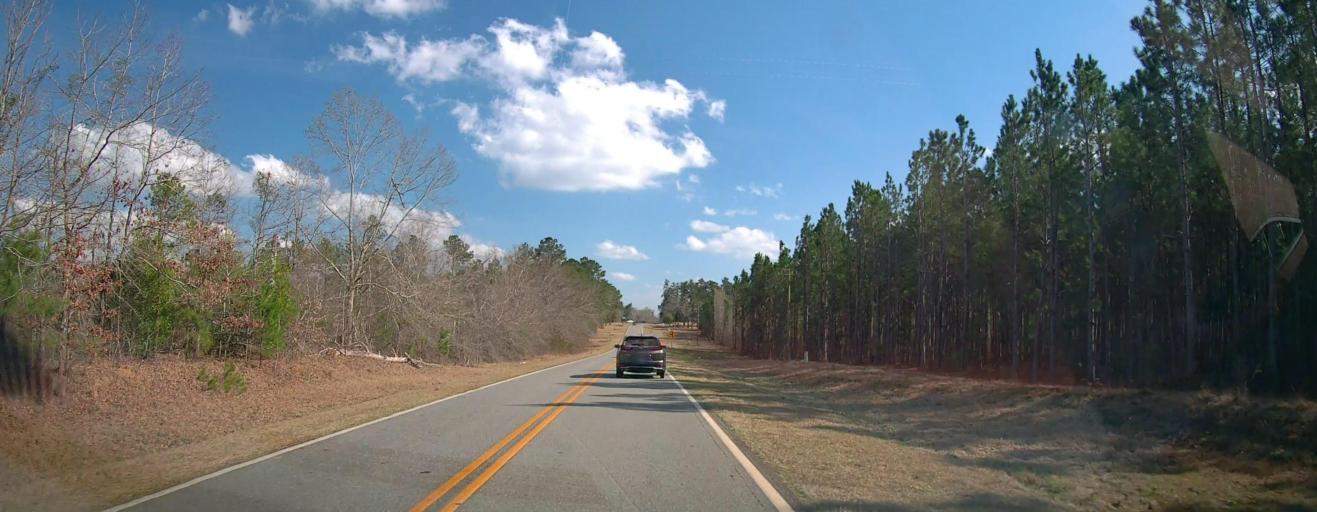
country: US
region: Georgia
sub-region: Laurens County
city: Dublin
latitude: 32.6215
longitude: -83.0892
